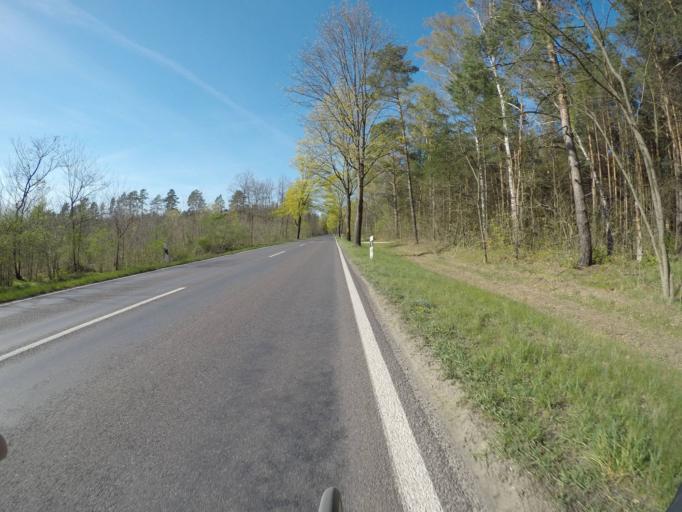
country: DE
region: Brandenburg
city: Grunheide
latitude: 52.4588
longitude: 13.8635
